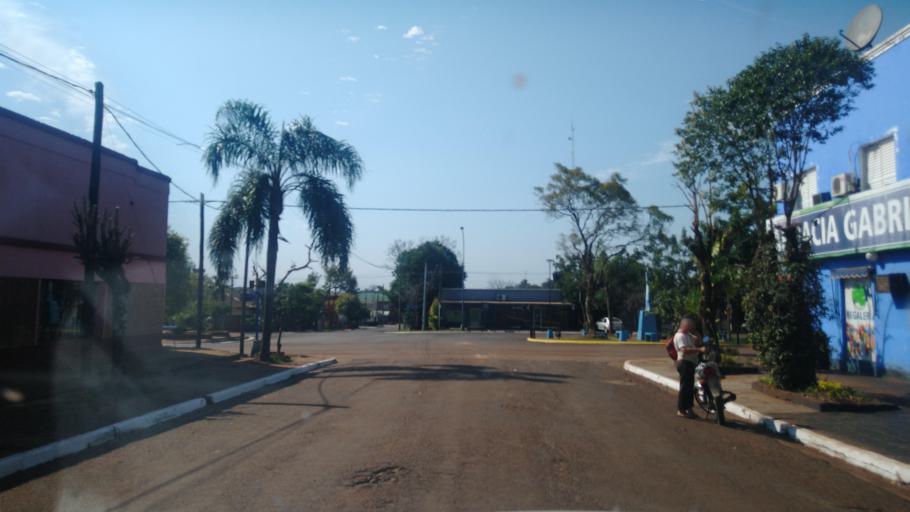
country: AR
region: Misiones
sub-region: Departamento de San Ignacio
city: San Ignacio
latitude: -27.2556
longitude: -55.5382
